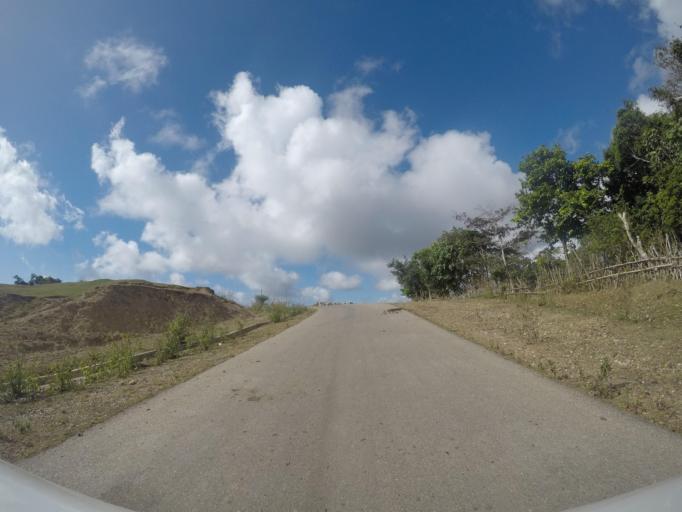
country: TL
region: Lautem
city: Lospalos
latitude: -8.4795
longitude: 126.8693
